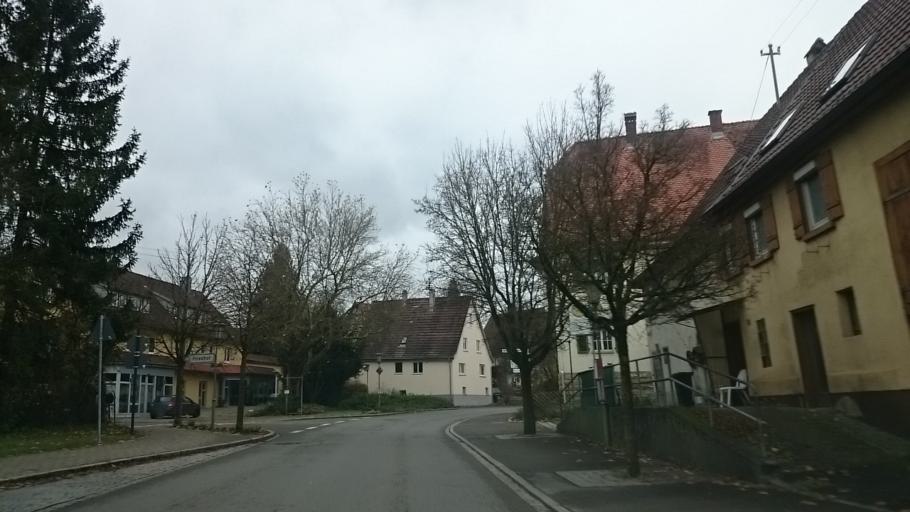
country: DE
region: Baden-Wuerttemberg
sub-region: Tuebingen Region
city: Mossingen
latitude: 48.3962
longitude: 9.0365
